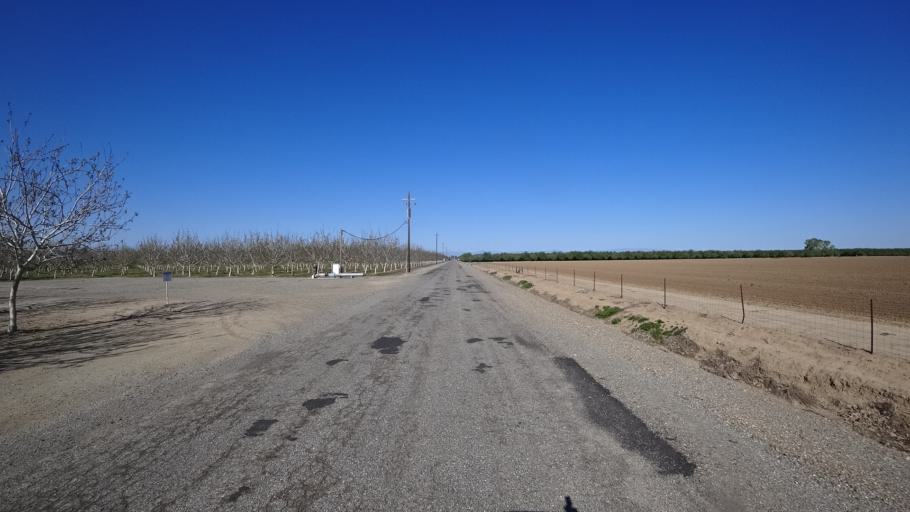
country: US
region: California
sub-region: Glenn County
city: Hamilton City
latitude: 39.6782
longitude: -122.0516
